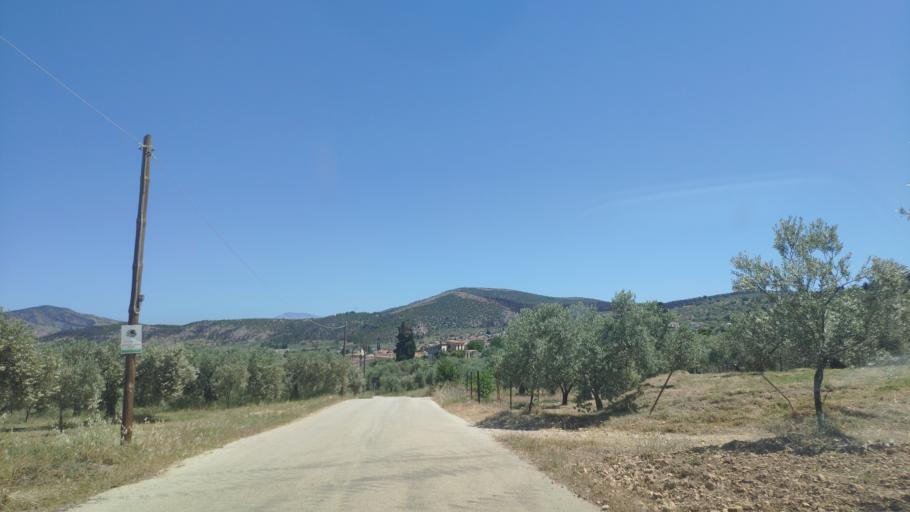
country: GR
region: Peloponnese
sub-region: Nomos Korinthias
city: Athikia
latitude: 37.8117
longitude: 22.9195
